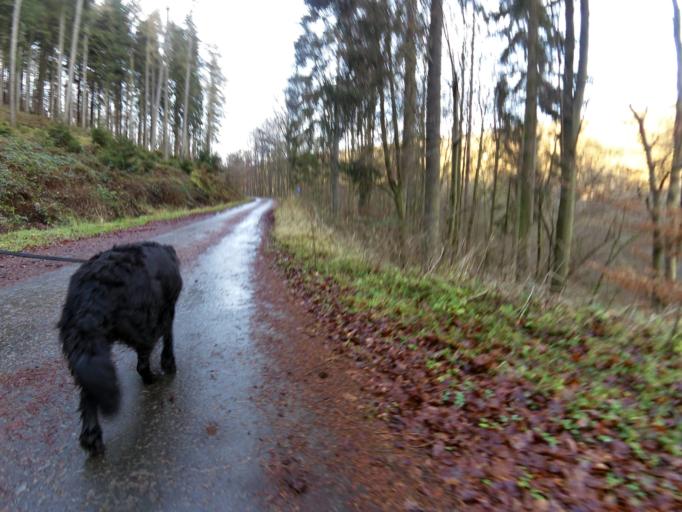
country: DE
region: Lower Saxony
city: Hannoversch Munden
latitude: 51.4641
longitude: 9.5972
